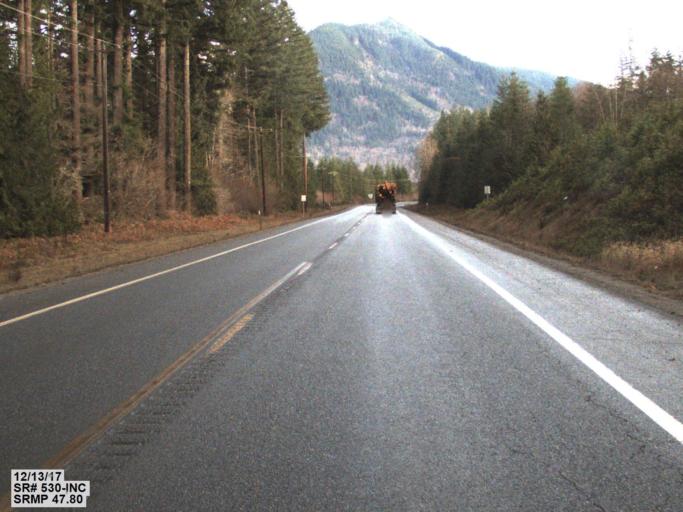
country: US
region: Washington
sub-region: Snohomish County
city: Darrington
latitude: 48.2622
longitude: -121.6265
